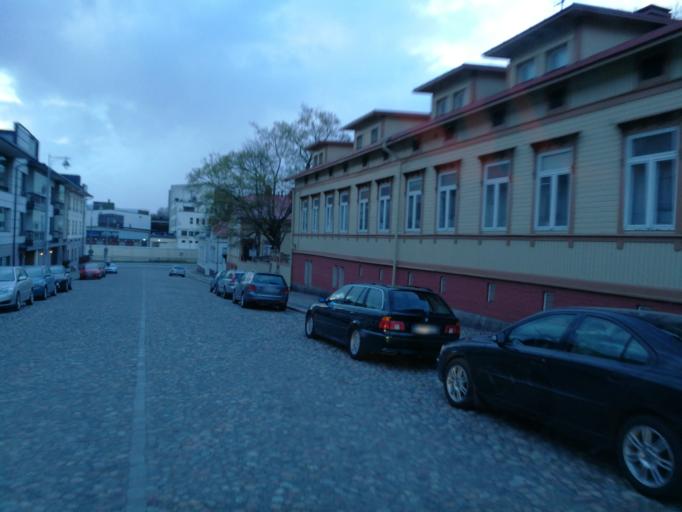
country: FI
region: Varsinais-Suomi
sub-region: Turku
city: Turku
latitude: 60.4451
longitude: 22.2390
